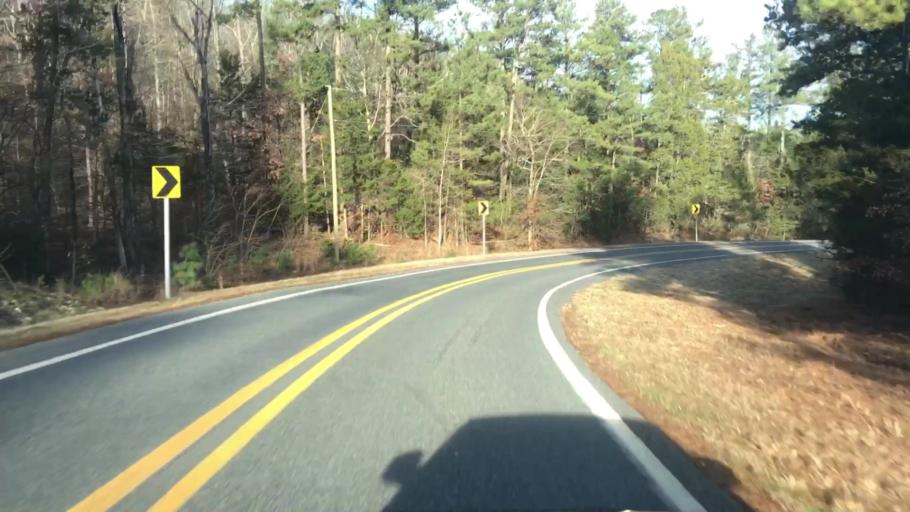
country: US
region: Arkansas
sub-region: Garland County
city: Rockwell
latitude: 34.4886
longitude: -93.2756
